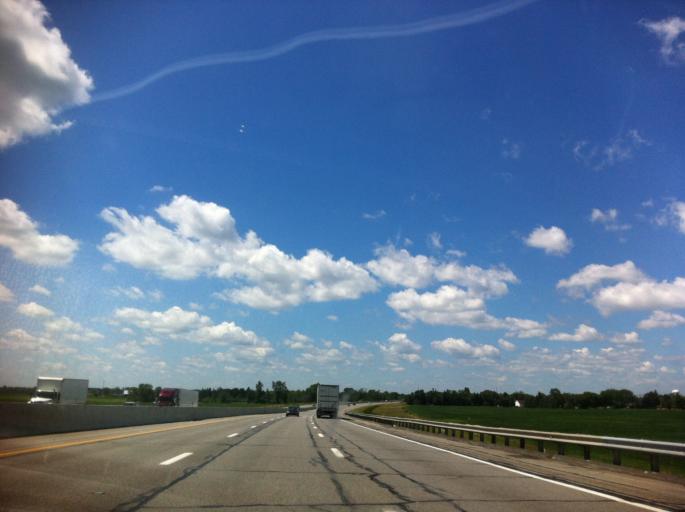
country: US
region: Ohio
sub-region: Wood County
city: Walbridge
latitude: 41.5403
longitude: -83.5139
